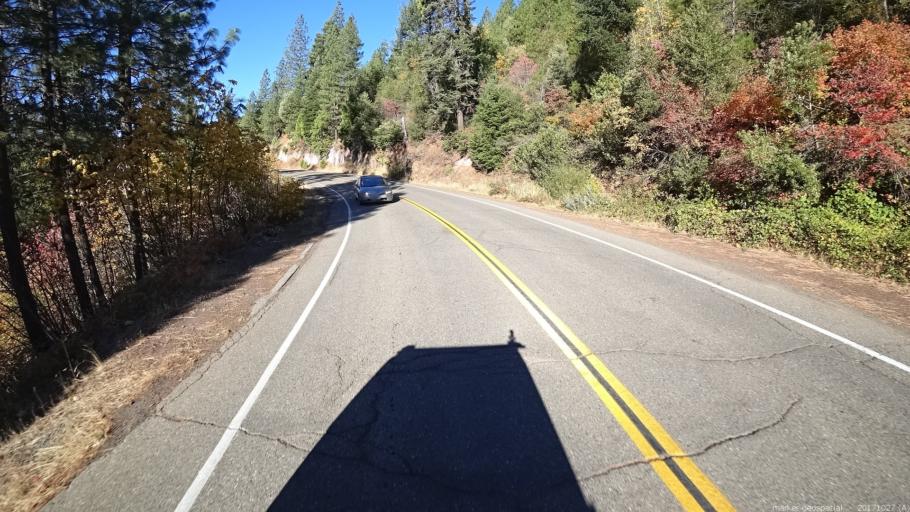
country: US
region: California
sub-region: Shasta County
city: Burney
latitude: 40.8729
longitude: -121.8960
